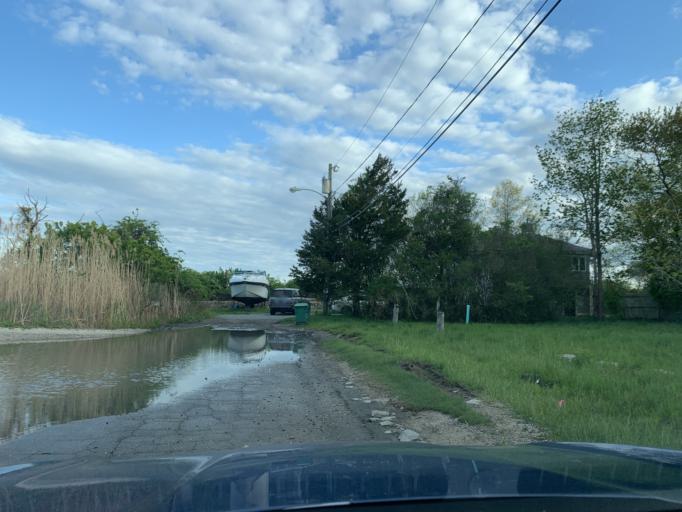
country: US
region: Rhode Island
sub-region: Kent County
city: Warwick
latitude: 41.6598
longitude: -71.4111
